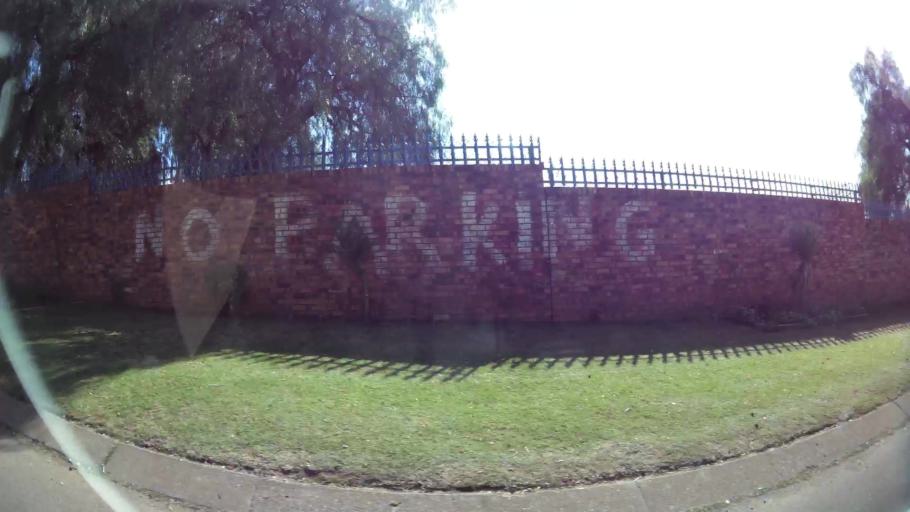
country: ZA
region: Gauteng
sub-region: City of Johannesburg Metropolitan Municipality
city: Soweto
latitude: -26.2475
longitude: 27.8847
